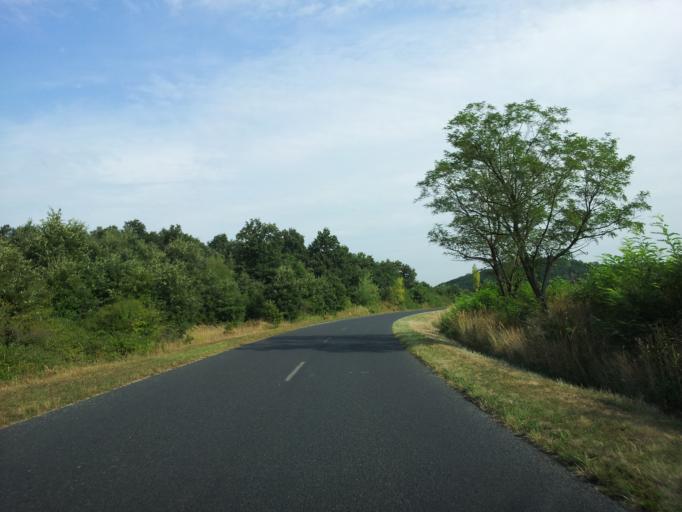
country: HU
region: Veszprem
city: Badacsonytomaj
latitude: 46.8490
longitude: 17.5503
